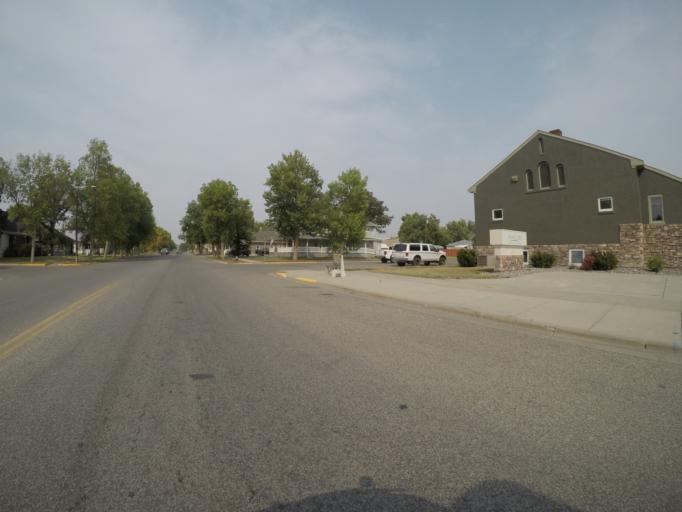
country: US
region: Montana
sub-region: Yellowstone County
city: Laurel
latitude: 45.6711
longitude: -108.7716
